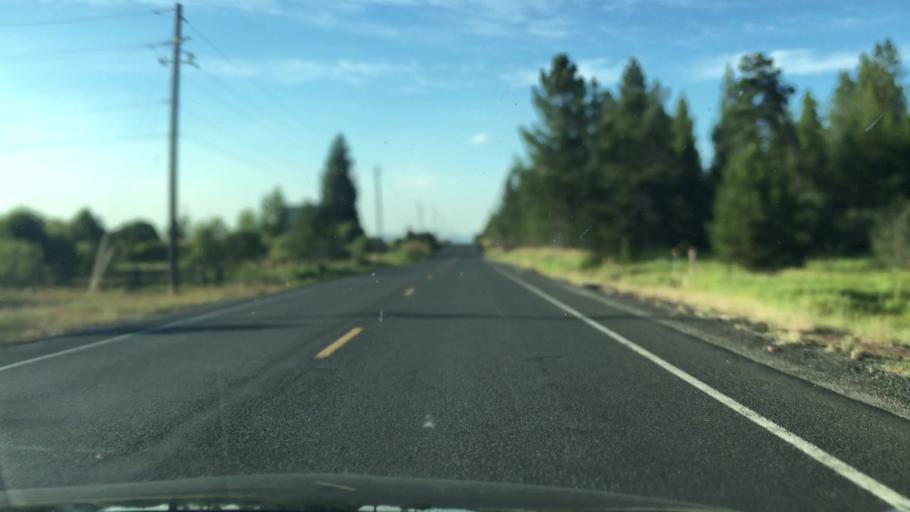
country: US
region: Idaho
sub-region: Valley County
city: McCall
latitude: 44.7925
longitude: -116.0782
